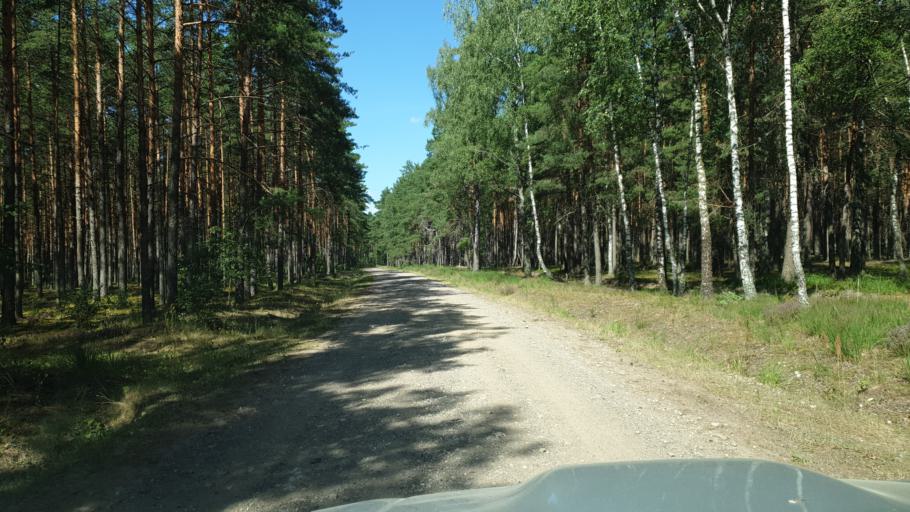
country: LT
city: Sirvintos
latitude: 54.9042
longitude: 24.9561
